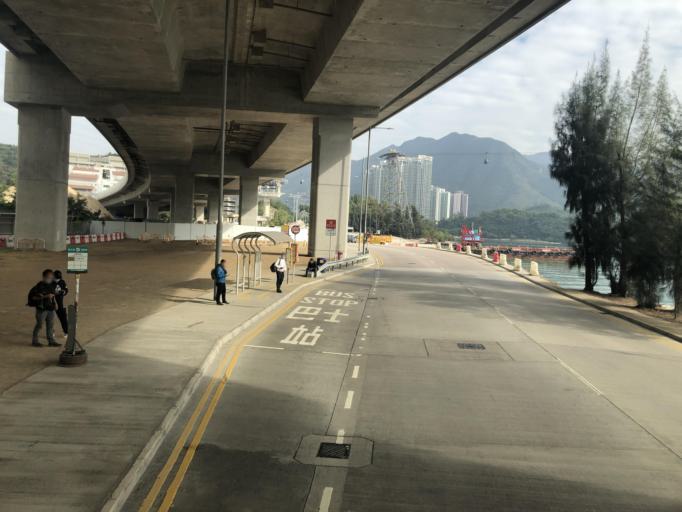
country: HK
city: Tai O
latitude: 22.2920
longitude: 113.9286
